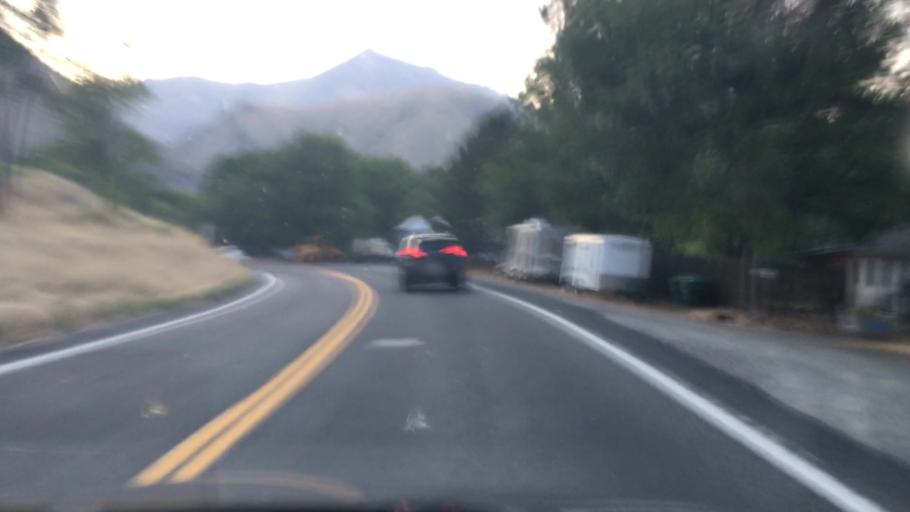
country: US
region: Idaho
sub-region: Idaho County
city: Grangeville
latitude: 45.4303
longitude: -116.3130
